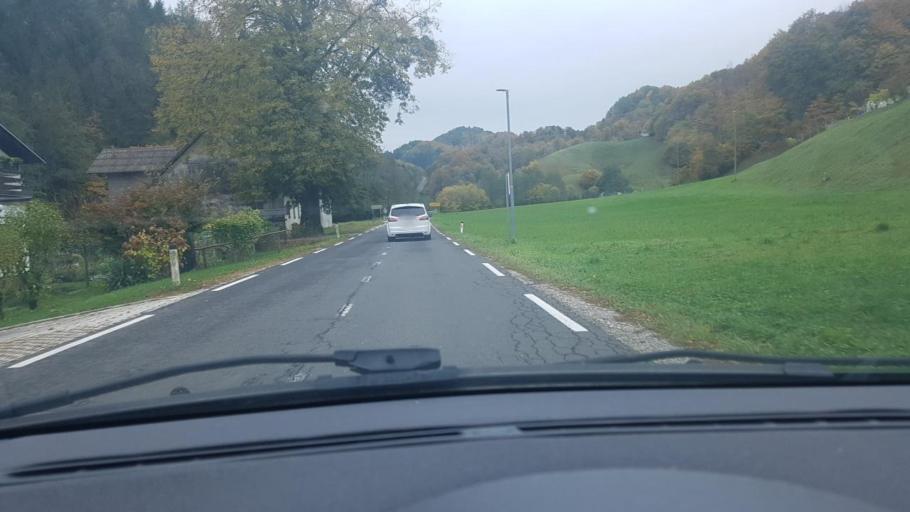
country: SI
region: Makole
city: Makole
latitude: 46.2848
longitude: 15.7137
